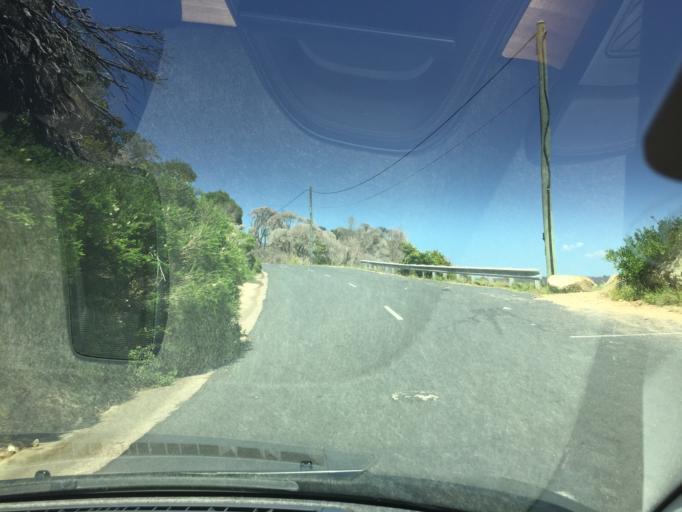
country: AU
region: New South Wales
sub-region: Bega Valley
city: Bega
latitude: -36.7257
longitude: 149.9888
